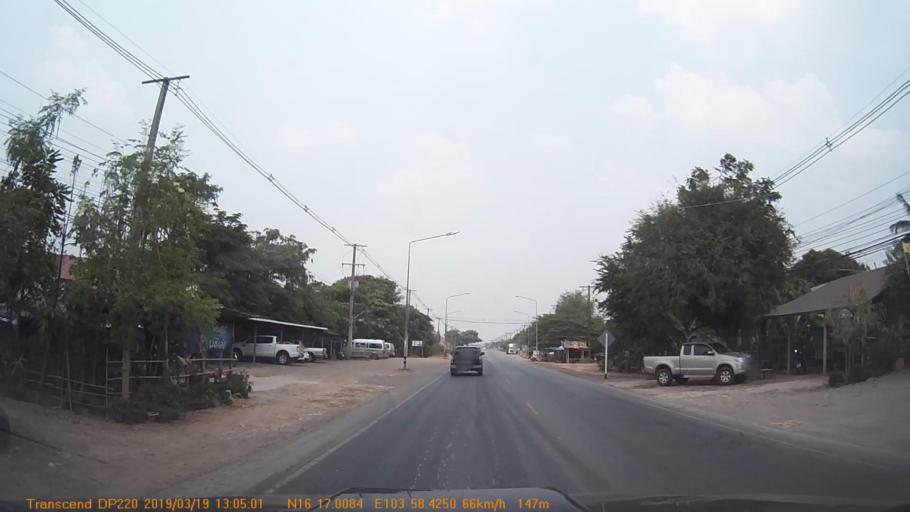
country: TH
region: Roi Et
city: Waeng
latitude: 16.2838
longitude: 103.9738
